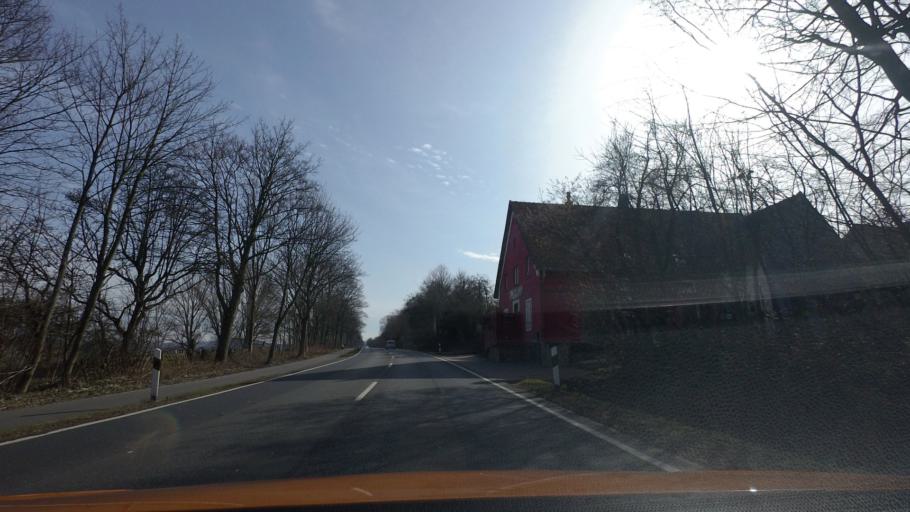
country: DE
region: Lower Saxony
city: Beckedorf
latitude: 52.3385
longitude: 9.3193
